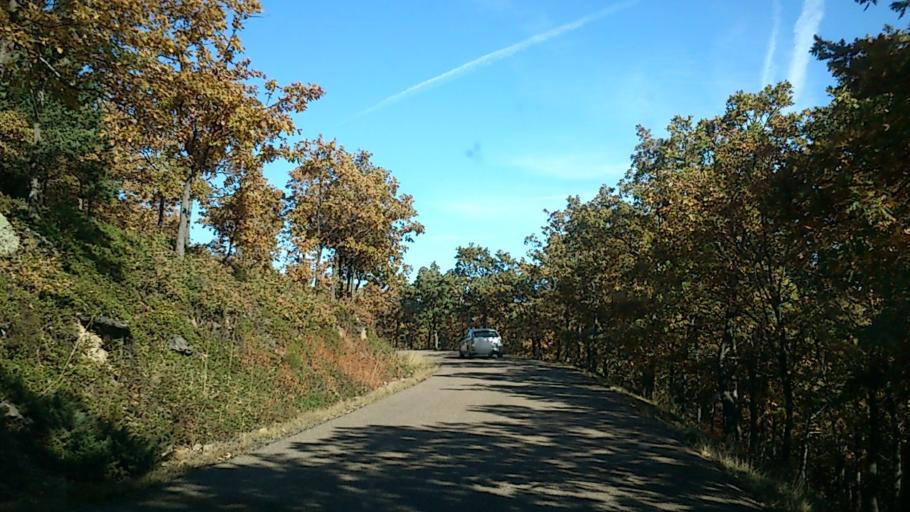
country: ES
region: Aragon
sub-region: Provincia de Zaragoza
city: Litago
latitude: 41.8056
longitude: -1.8005
